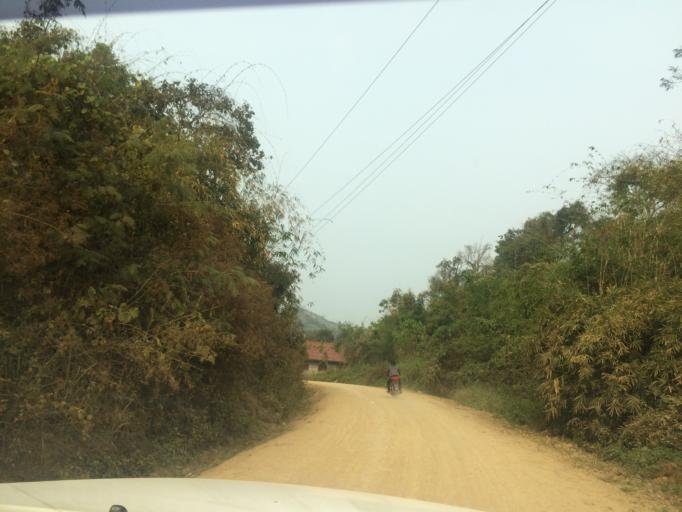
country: LA
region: Loungnamtha
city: Muang Nale
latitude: 20.4301
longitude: 101.7086
